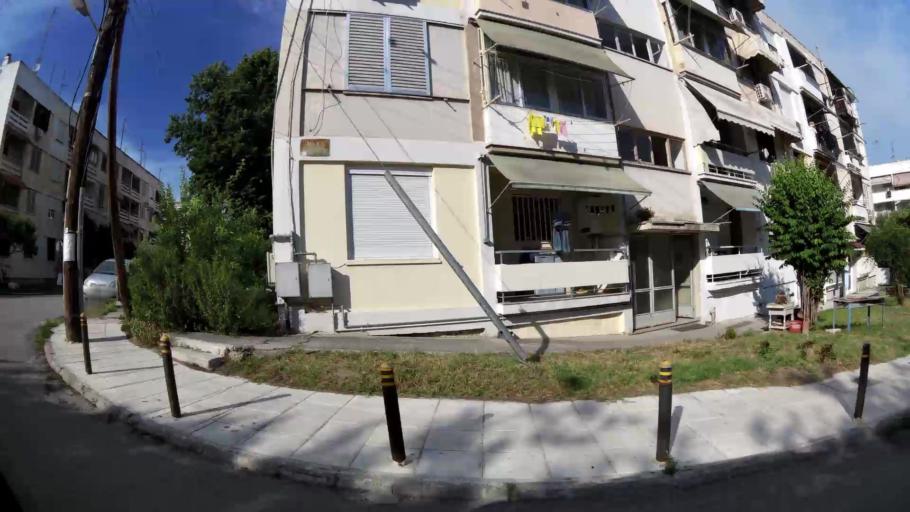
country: GR
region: Central Macedonia
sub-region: Nomos Thessalonikis
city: Kalamaria
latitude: 40.5708
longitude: 22.9704
